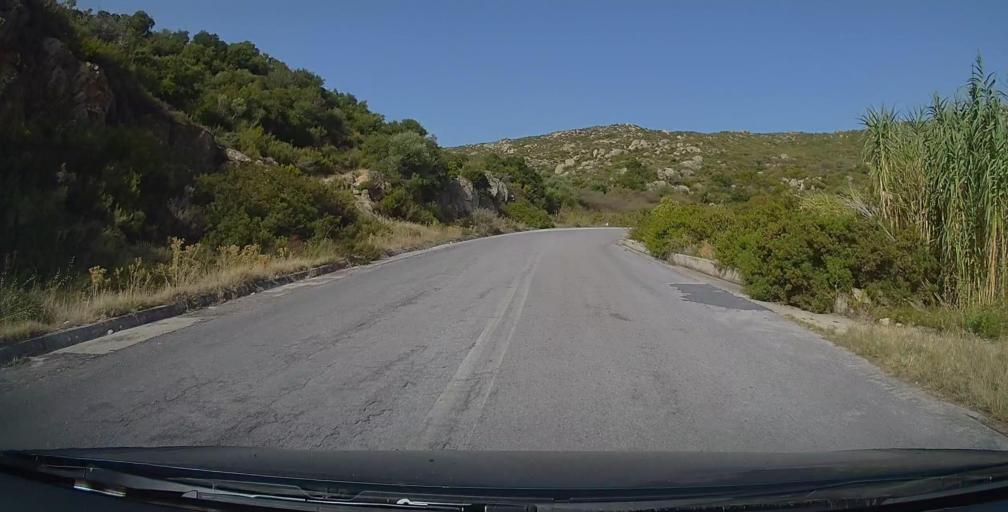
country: GR
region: Central Macedonia
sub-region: Nomos Chalkidikis
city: Sykia
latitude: 39.9978
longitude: 23.9854
